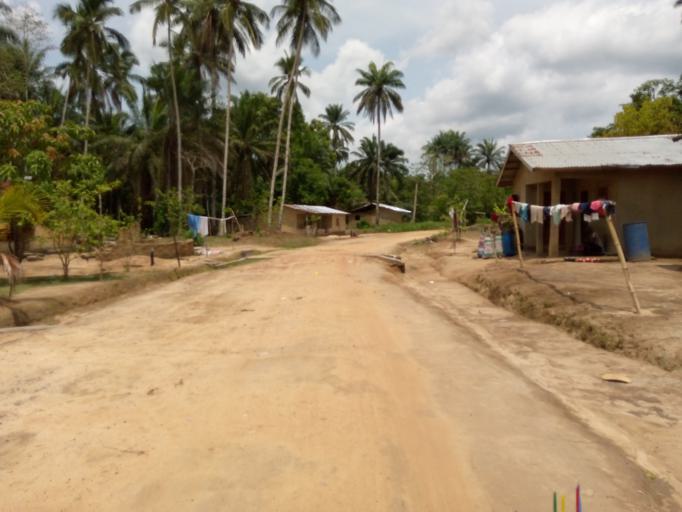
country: SL
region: Western Area
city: Waterloo
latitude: 8.3124
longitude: -12.9420
